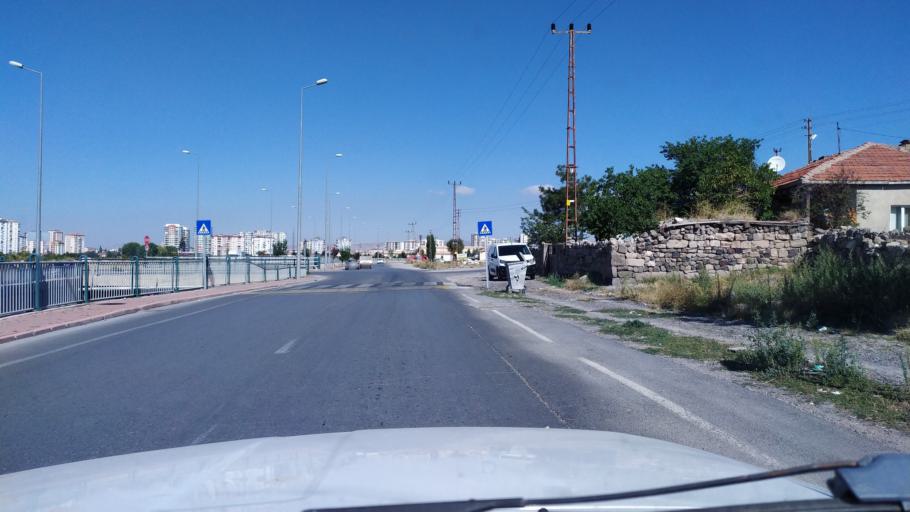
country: TR
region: Kayseri
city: Talas
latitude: 38.7338
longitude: 35.5482
